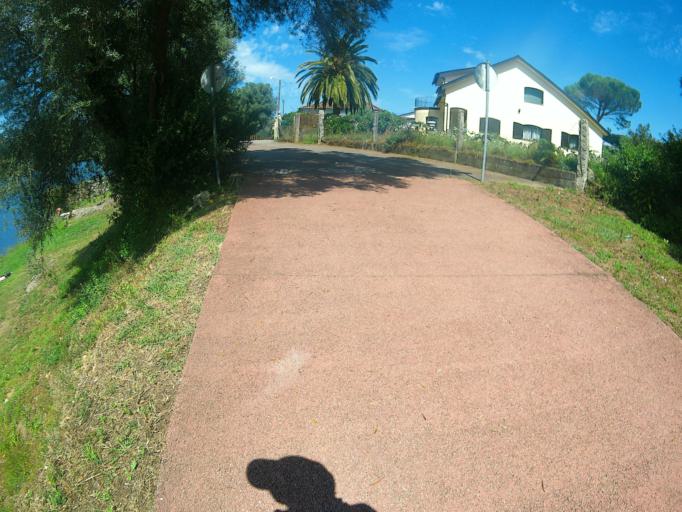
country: PT
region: Viana do Castelo
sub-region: Valenca
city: Valenca
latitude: 41.9956
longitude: -8.6722
